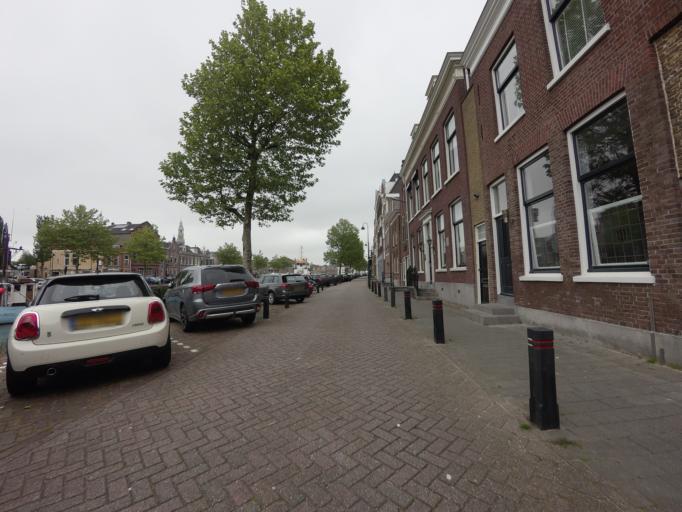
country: NL
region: South Holland
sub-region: Gemeente Maassluis
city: Maassluis
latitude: 51.9193
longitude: 4.2504
